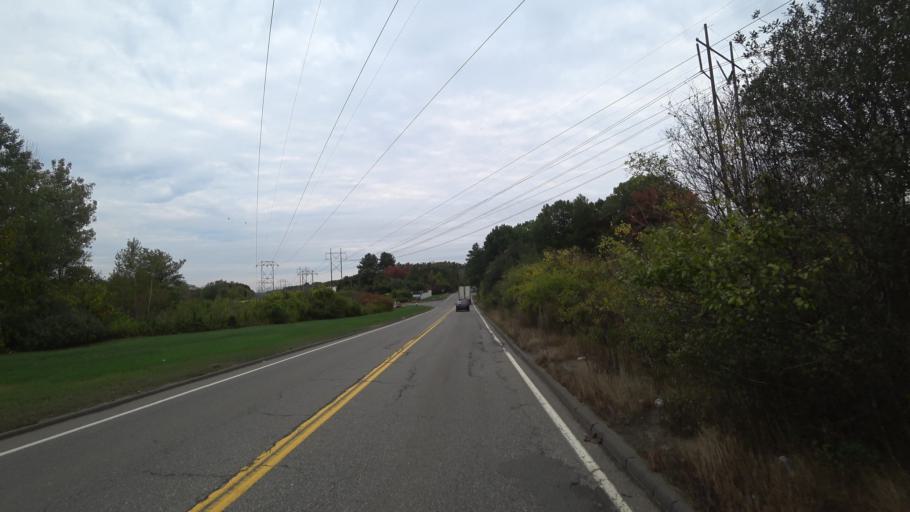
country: US
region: Massachusetts
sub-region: Middlesex County
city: Wilmington
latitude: 42.5969
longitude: -71.1623
